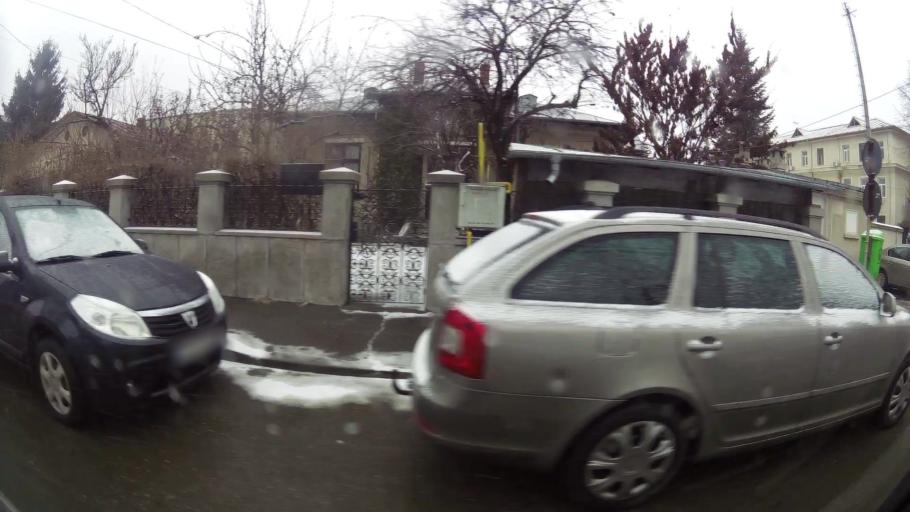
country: RO
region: Prahova
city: Ploiesti
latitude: 44.9400
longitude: 26.0111
